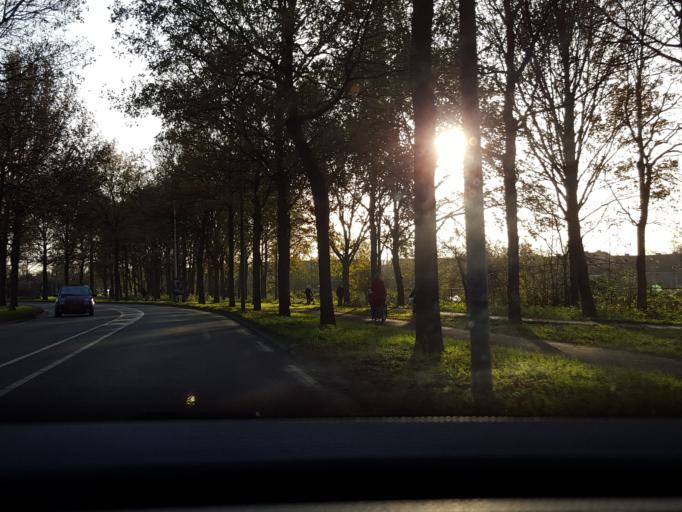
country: NL
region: Gelderland
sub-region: Gemeente Zutphen
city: Zutphen
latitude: 52.1304
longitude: 6.1958
